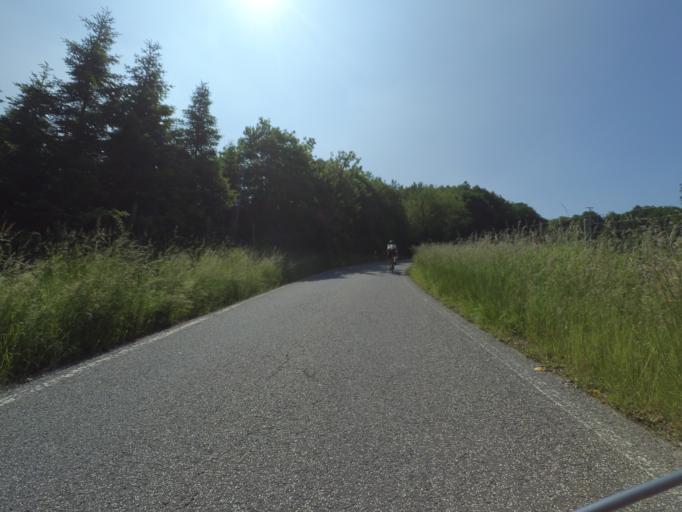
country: DE
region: Rheinland-Pfalz
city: Brodenbach
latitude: 50.2227
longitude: 7.4533
